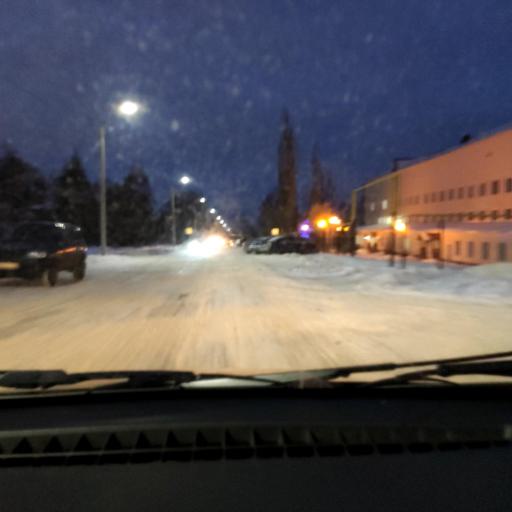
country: RU
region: Bashkortostan
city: Blagoveshchensk
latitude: 55.0473
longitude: 55.9486
